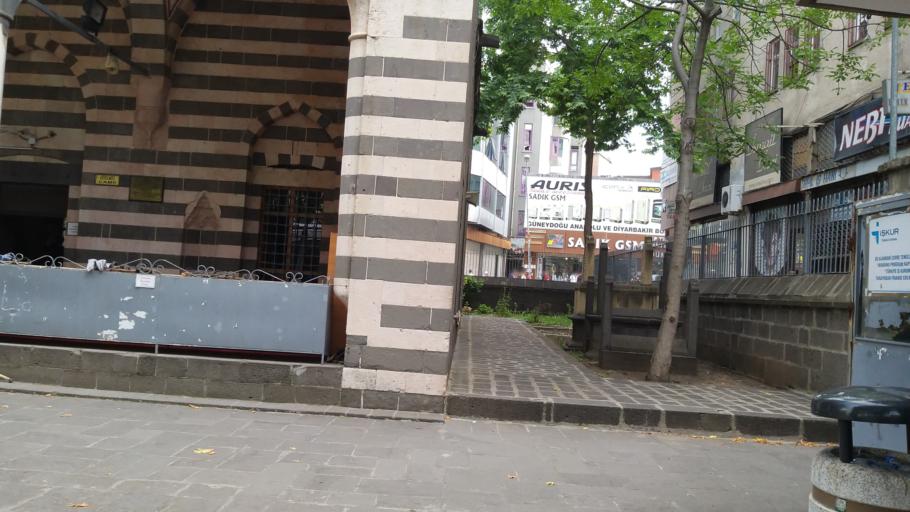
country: TR
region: Diyarbakir
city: Sur
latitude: 37.9152
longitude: 40.2365
